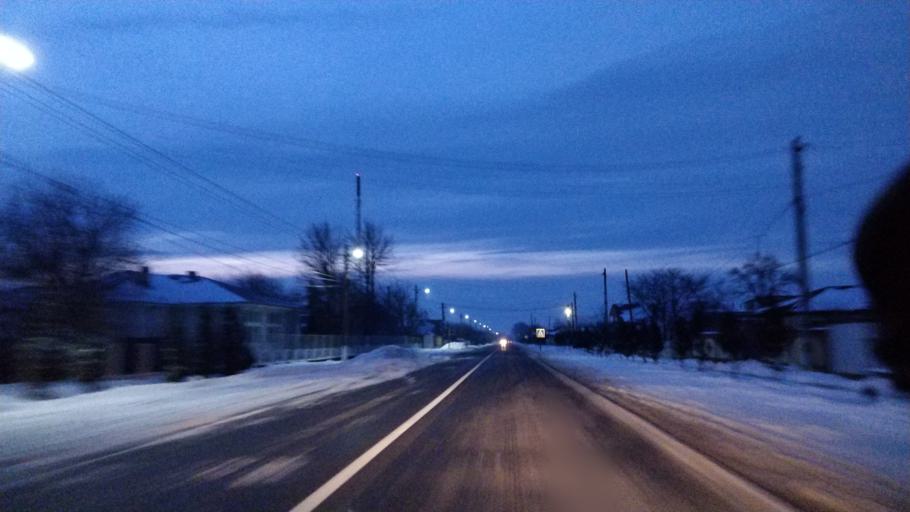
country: RO
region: Vrancea
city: Vulturu de Sus
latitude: 45.6349
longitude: 27.3812
